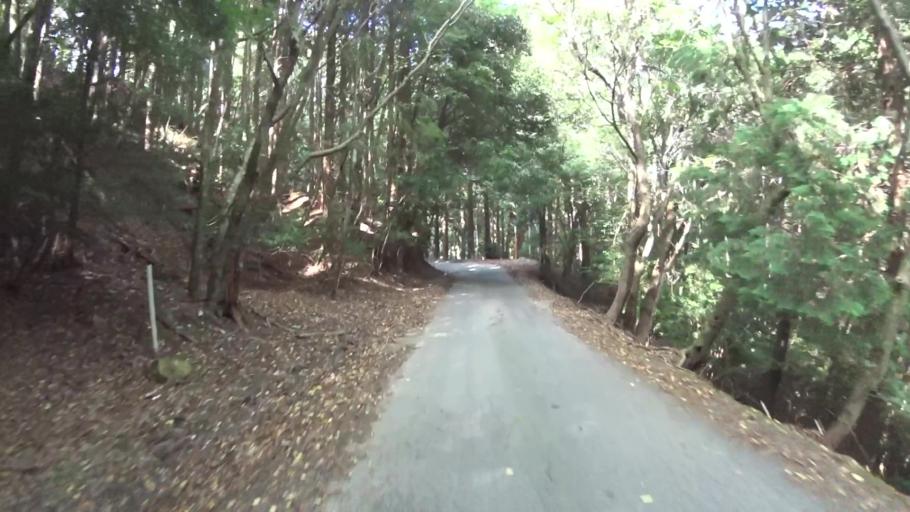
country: JP
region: Shiga Prefecture
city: Otsu-shi
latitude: 34.9507
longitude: 135.8392
